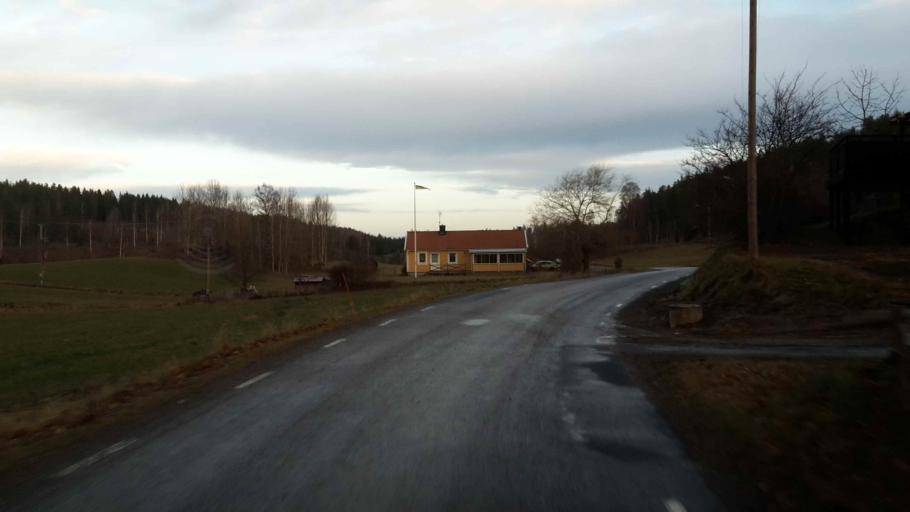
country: SE
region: Kalmar
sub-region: Vasterviks Kommun
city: Overum
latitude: 58.1583
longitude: 16.3304
